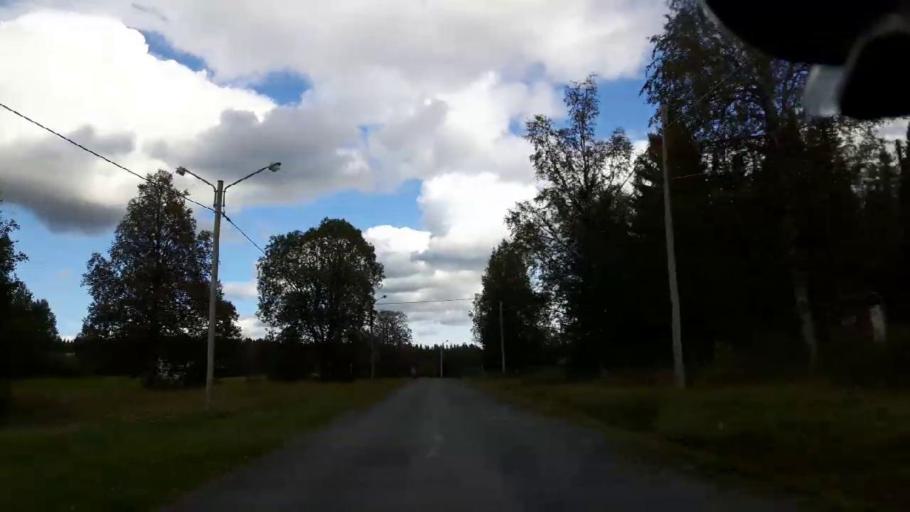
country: SE
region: Jaemtland
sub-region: Stroemsunds Kommun
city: Stroemsund
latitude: 63.4194
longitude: 15.8409
